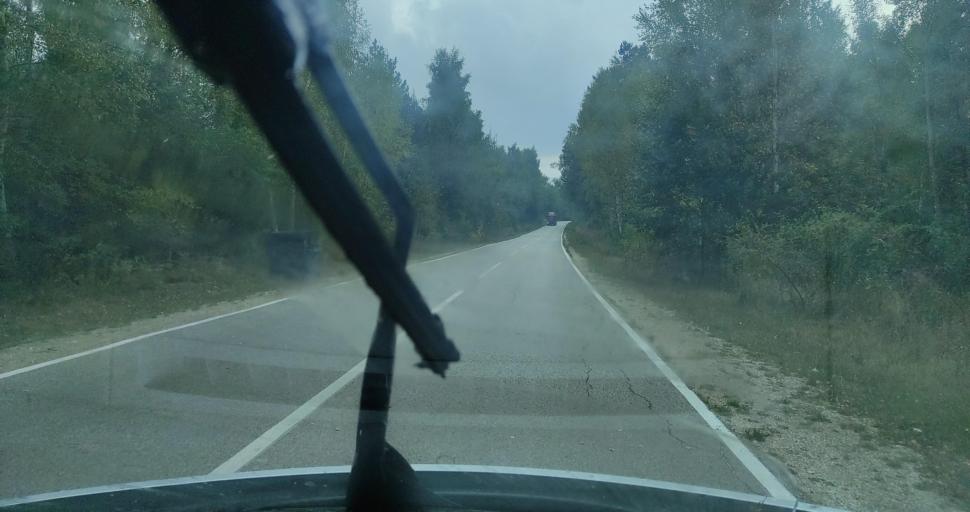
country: RS
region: Central Serbia
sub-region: Jablanicki Okrug
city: Crna Trava
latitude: 42.7280
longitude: 22.3360
